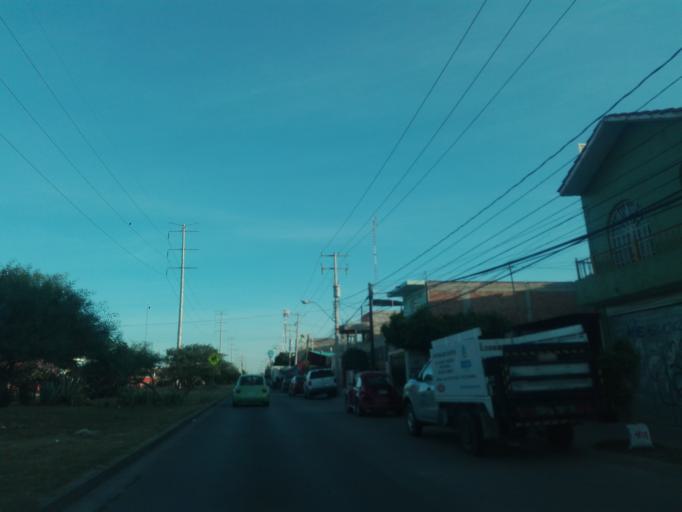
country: MX
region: Guanajuato
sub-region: Leon
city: Fraccionamiento Paraiso Real
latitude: 21.0803
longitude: -101.6227
